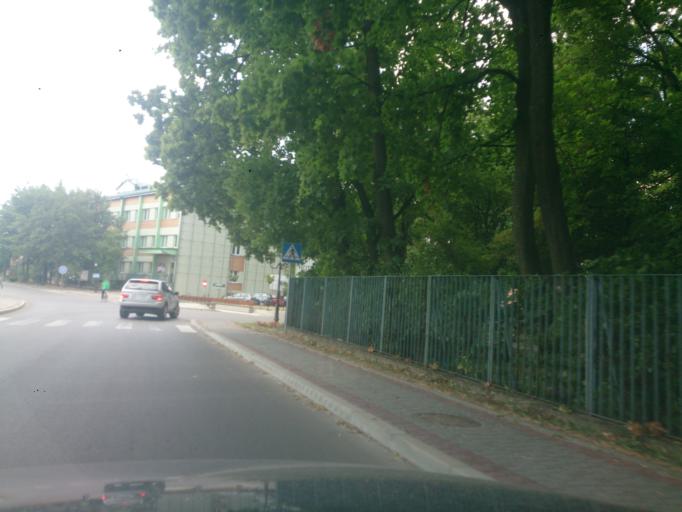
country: PL
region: Subcarpathian Voivodeship
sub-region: Powiat tarnobrzeski
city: Baranow Sandomierski
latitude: 50.5007
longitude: 21.5340
